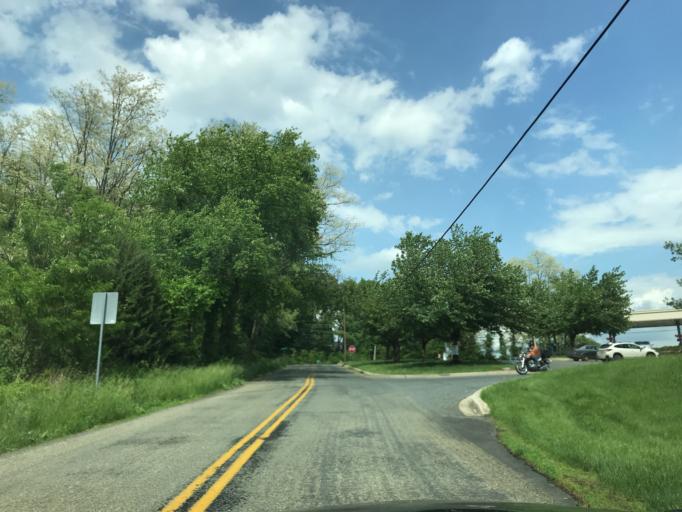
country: US
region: Maryland
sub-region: Harford County
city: Jarrettsville
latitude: 39.6722
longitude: -76.4109
